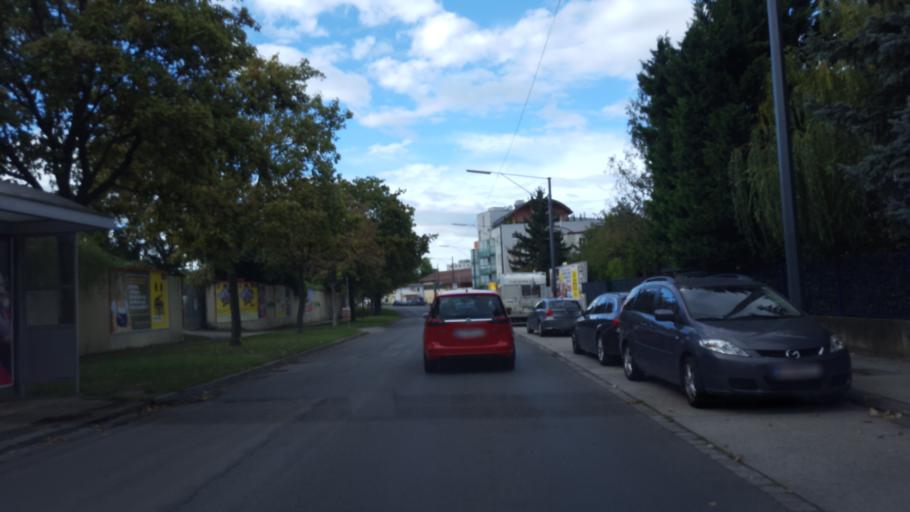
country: AT
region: Lower Austria
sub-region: Politischer Bezirk Wien-Umgebung
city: Schwechat
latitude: 48.1609
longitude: 16.4225
